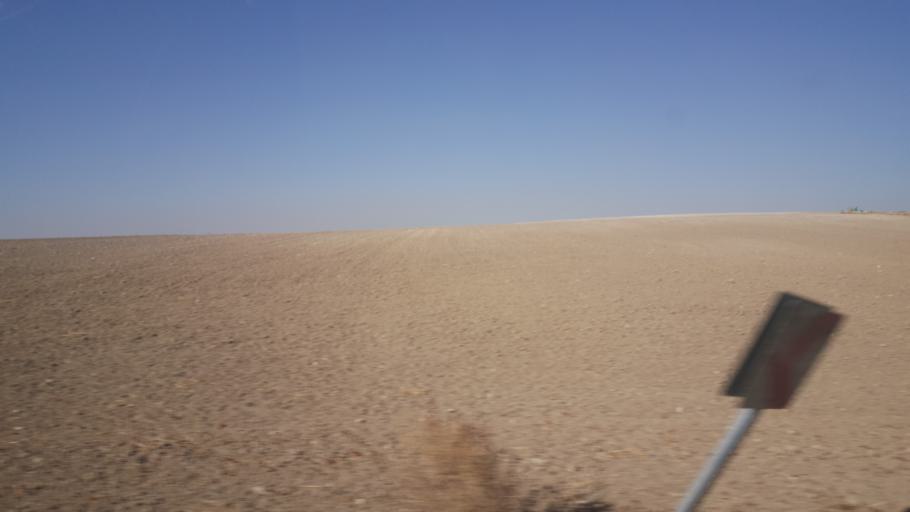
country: TR
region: Konya
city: Celtik
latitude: 39.0622
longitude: 31.8746
